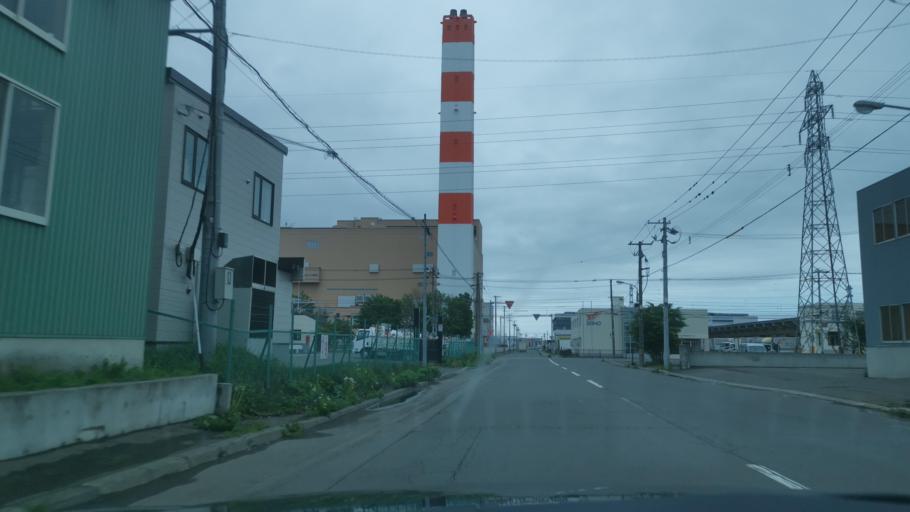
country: JP
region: Hokkaido
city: Sapporo
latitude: 43.1084
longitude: 141.2850
